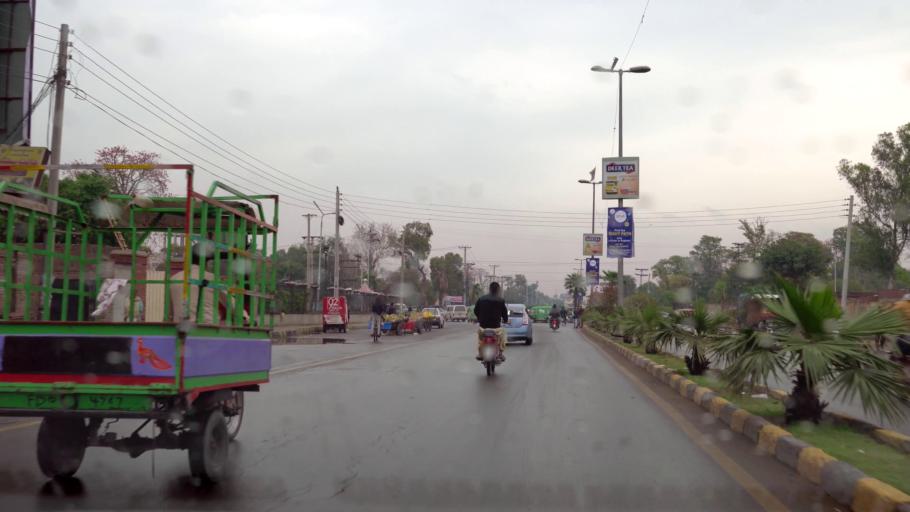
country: PK
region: Punjab
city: Faisalabad
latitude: 31.4198
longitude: 73.0852
